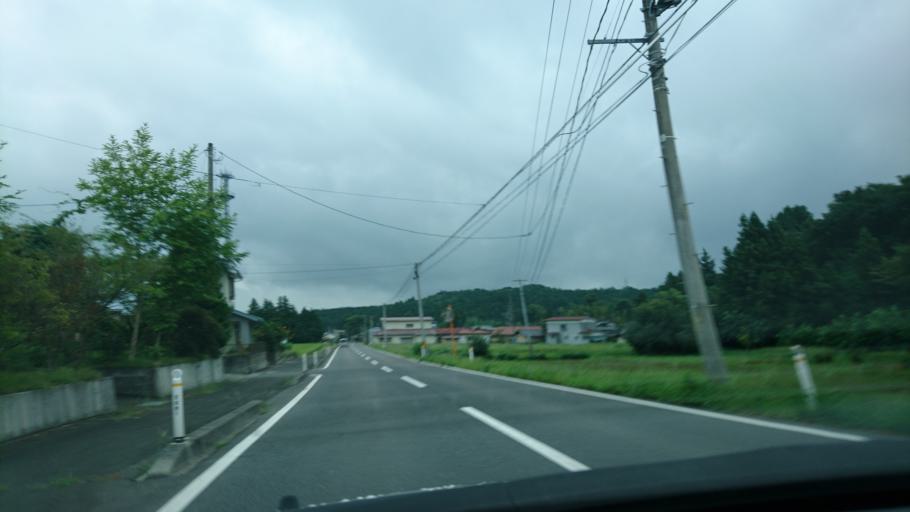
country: JP
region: Iwate
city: Ichinoseki
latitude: 38.8050
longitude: 140.9351
